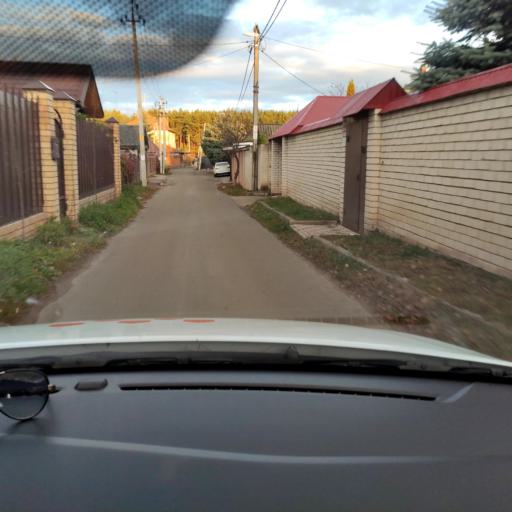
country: RU
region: Tatarstan
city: Verkhniy Uslon
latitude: 55.6218
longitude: 49.0148
